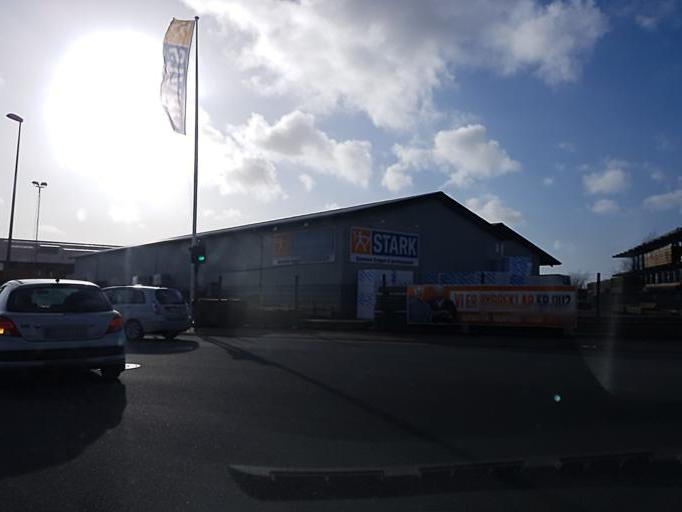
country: DK
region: Central Jutland
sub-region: Holstebro Kommune
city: Holstebro
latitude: 56.3796
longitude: 8.6210
